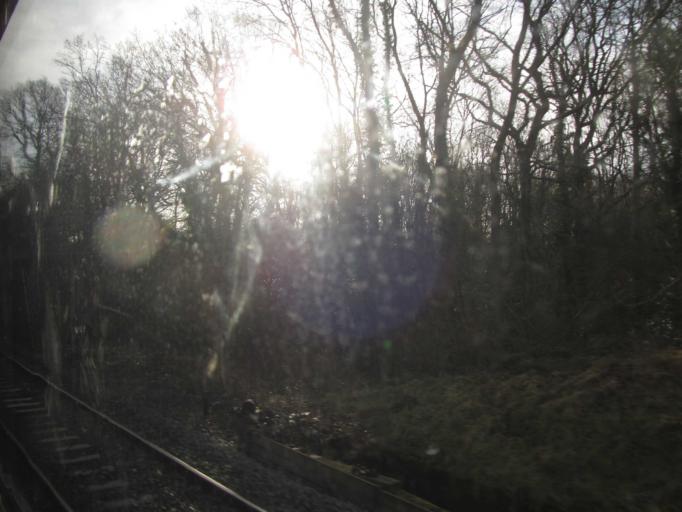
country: GB
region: England
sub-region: Surrey
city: Normandy
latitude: 51.2439
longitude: -0.6942
